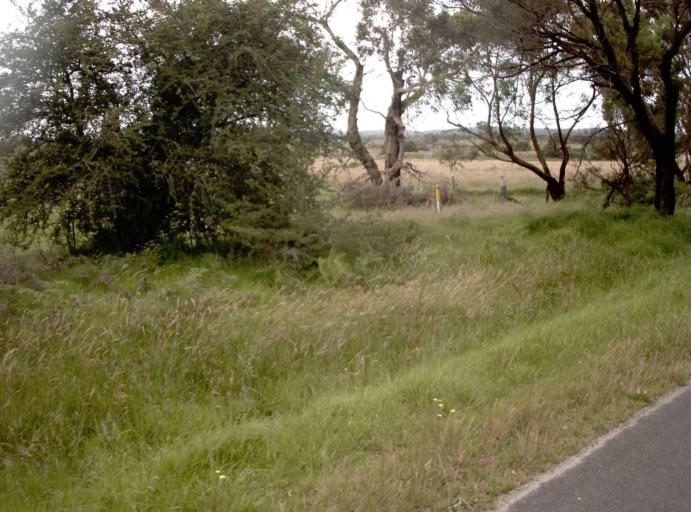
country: AU
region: Victoria
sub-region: Cardinia
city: Koo-Wee-Rup
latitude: -38.2951
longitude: 145.5566
